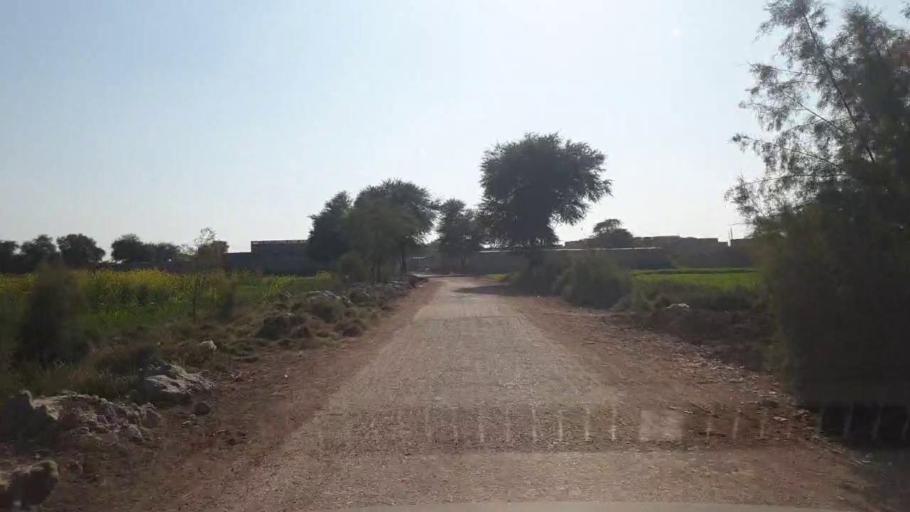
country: PK
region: Sindh
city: Shahpur Chakar
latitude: 26.1476
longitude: 68.6765
